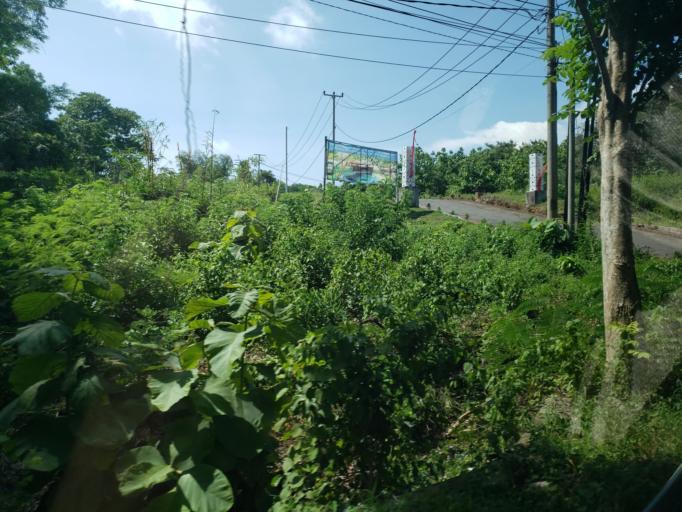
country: ID
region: Bali
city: Kangin
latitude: -8.8251
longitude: 115.1514
